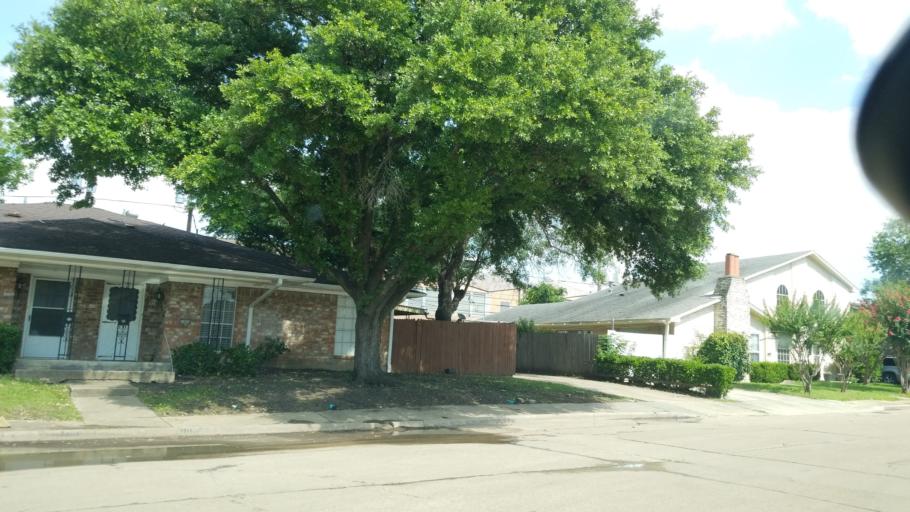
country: US
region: Texas
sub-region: Dallas County
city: Farmers Branch
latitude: 32.8820
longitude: -96.8583
